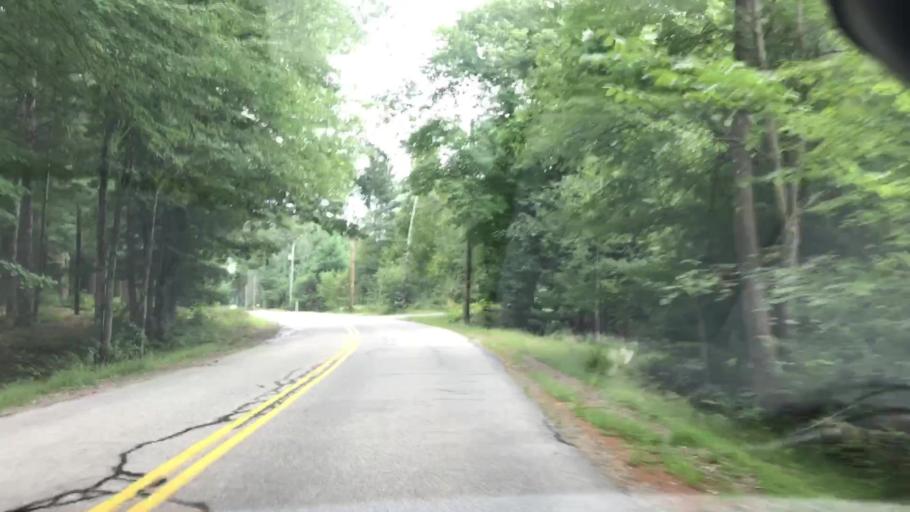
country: US
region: New Hampshire
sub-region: Hillsborough County
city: Merrimack
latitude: 42.8499
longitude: -71.5704
